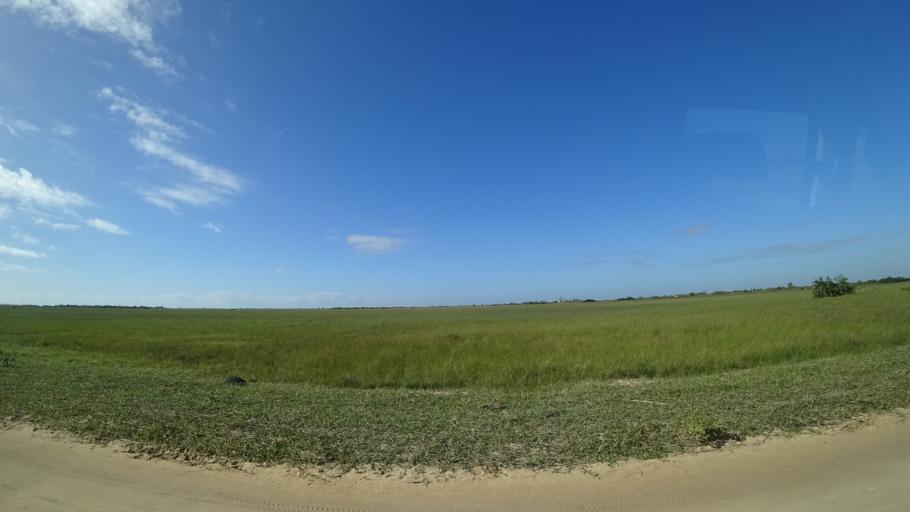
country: MZ
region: Sofala
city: Beira
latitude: -19.7294
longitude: 34.9831
